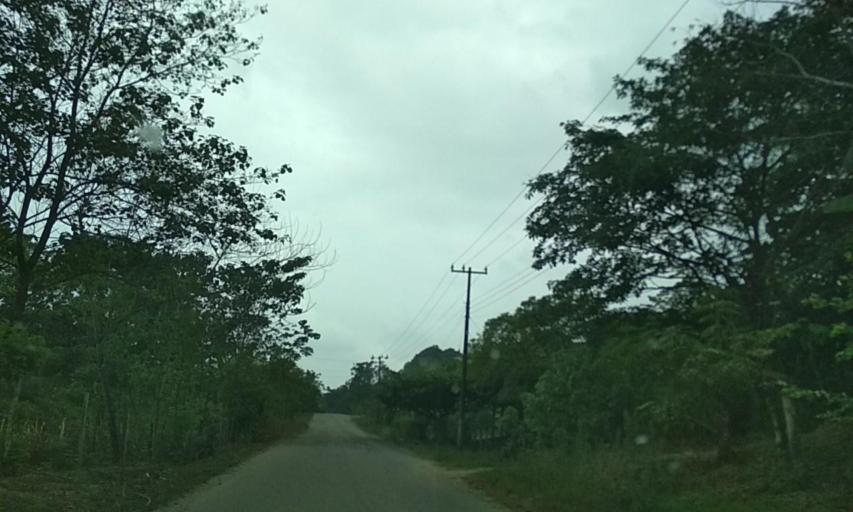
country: MX
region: Veracruz
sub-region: Uxpanapa
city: Poblado 10
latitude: 17.4596
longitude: -94.1040
